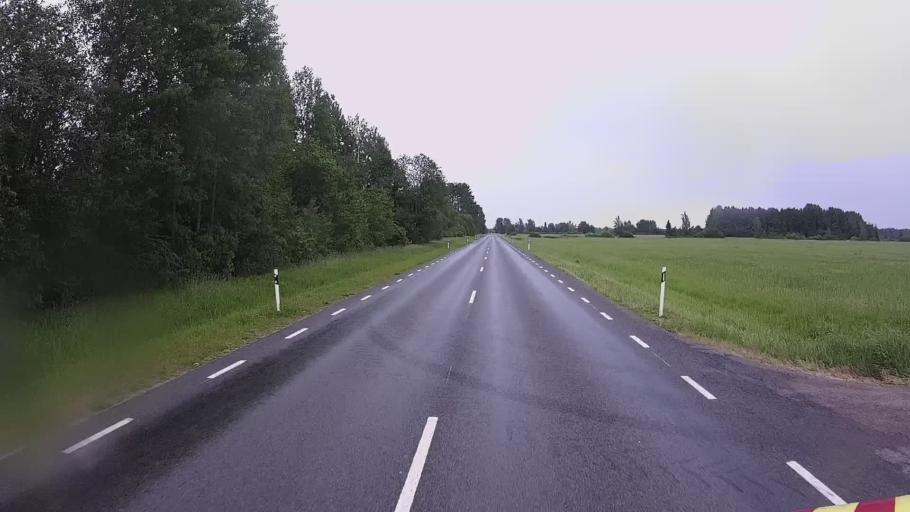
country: EE
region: Paernumaa
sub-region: Vaendra vald (alev)
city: Vandra
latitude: 58.5901
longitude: 25.1624
